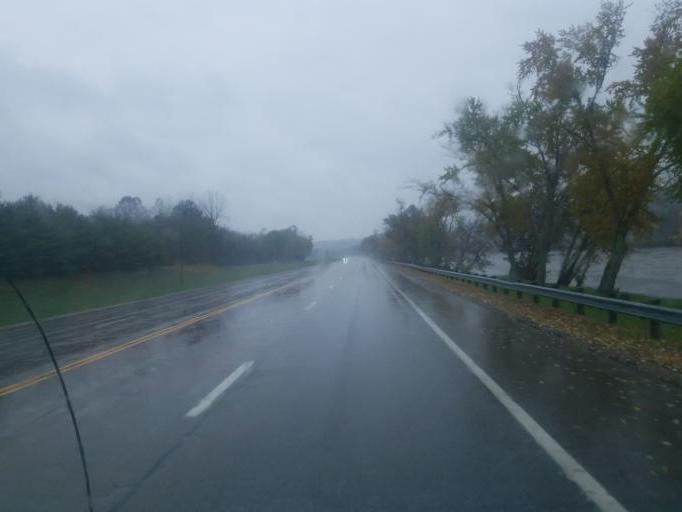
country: US
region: Ohio
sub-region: Muskingum County
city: South Zanesville
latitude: 39.8760
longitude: -81.9668
